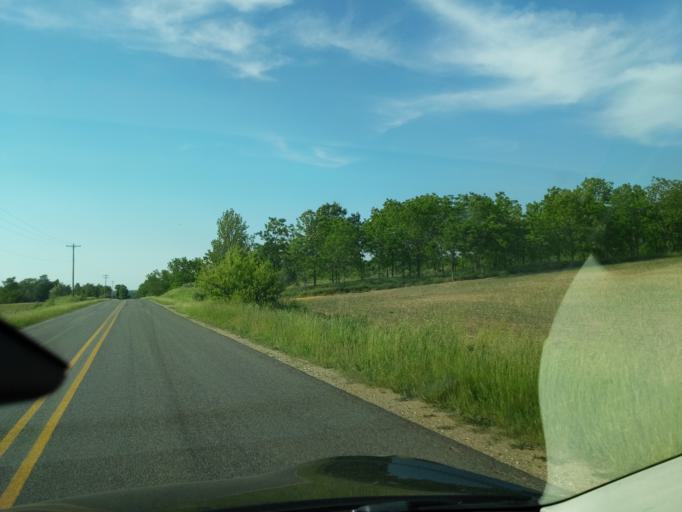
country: US
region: Michigan
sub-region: Barry County
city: Nashville
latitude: 42.6079
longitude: -85.1539
